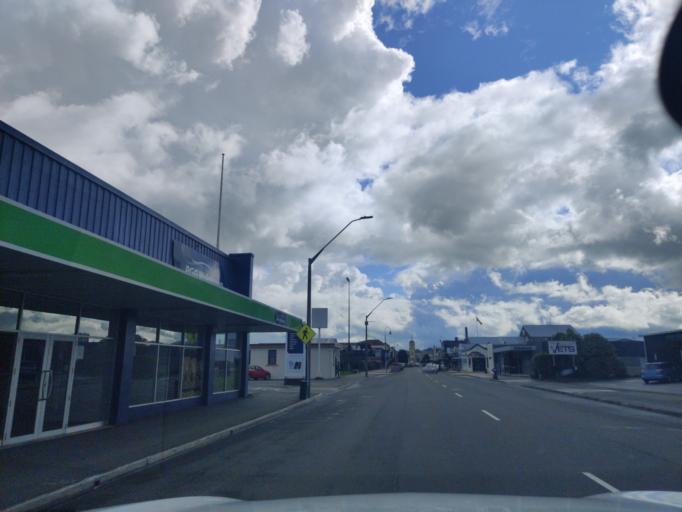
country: NZ
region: Manawatu-Wanganui
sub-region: Palmerston North City
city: Palmerston North
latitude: -40.2290
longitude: 175.5666
